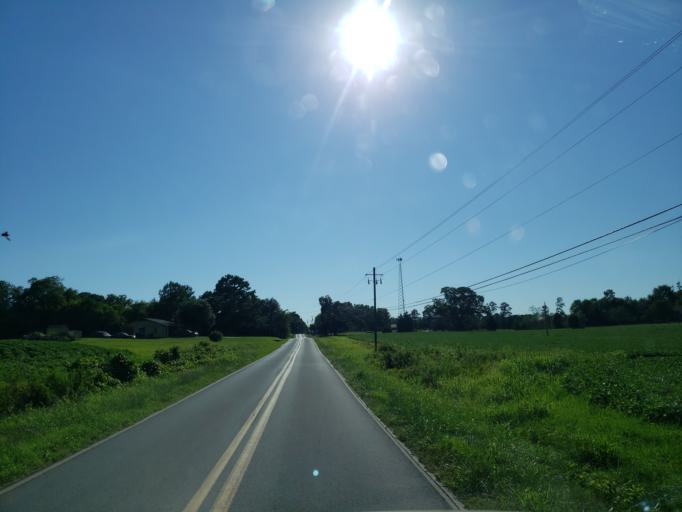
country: US
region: Georgia
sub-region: Bartow County
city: Euharlee
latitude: 34.1086
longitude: -84.9227
